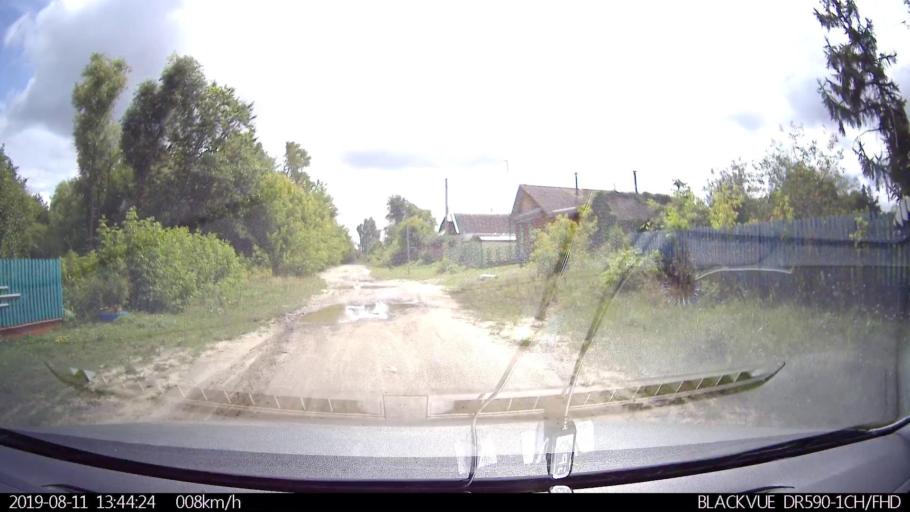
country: RU
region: Ulyanovsk
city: Ignatovka
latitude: 53.8533
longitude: 47.5744
